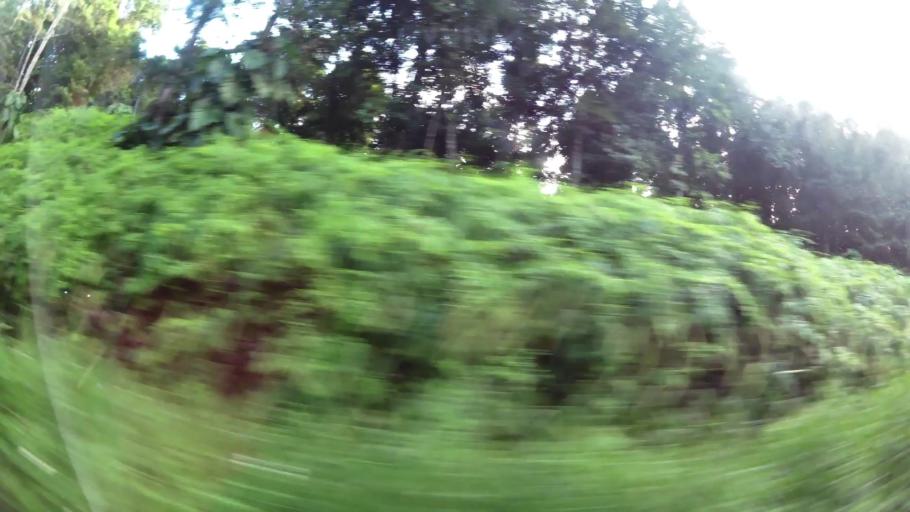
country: GP
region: Guadeloupe
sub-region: Guadeloupe
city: Bouillante
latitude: 16.1787
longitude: -61.7075
